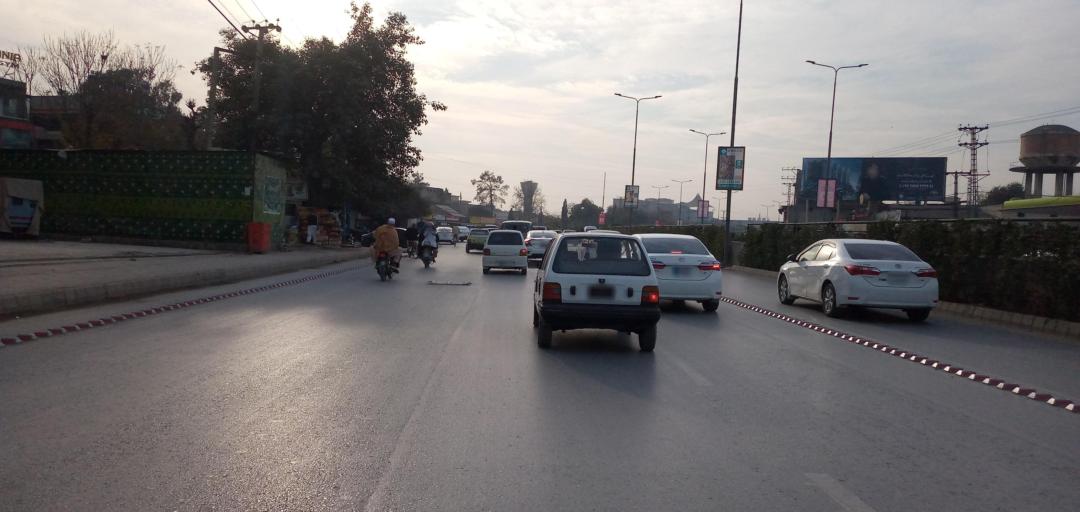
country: PK
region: Khyber Pakhtunkhwa
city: Peshawar
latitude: 33.9982
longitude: 71.4928
